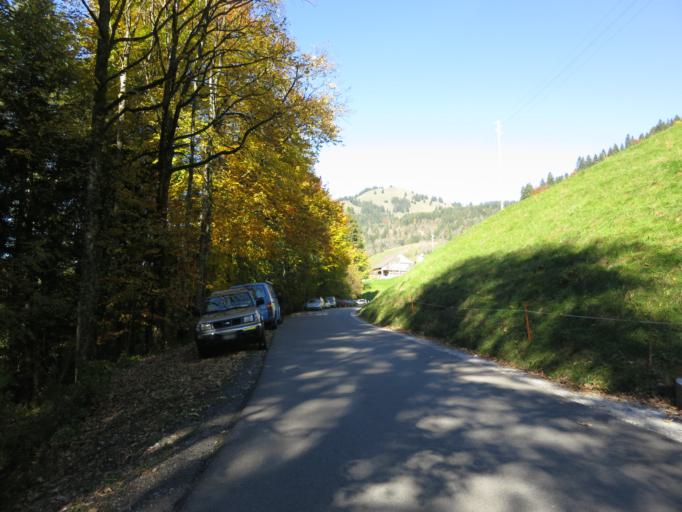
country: CH
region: Schwyz
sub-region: Bezirk March
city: Vorderthal
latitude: 47.0874
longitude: 8.9308
